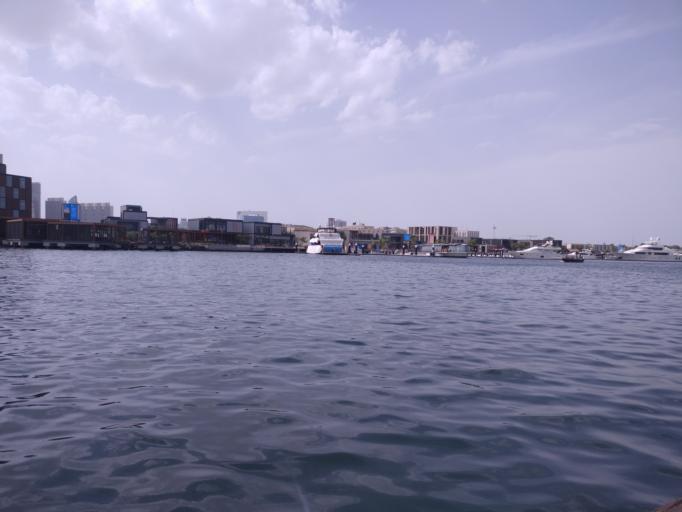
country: AE
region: Ash Shariqah
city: Sharjah
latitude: 25.2575
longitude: 55.3143
